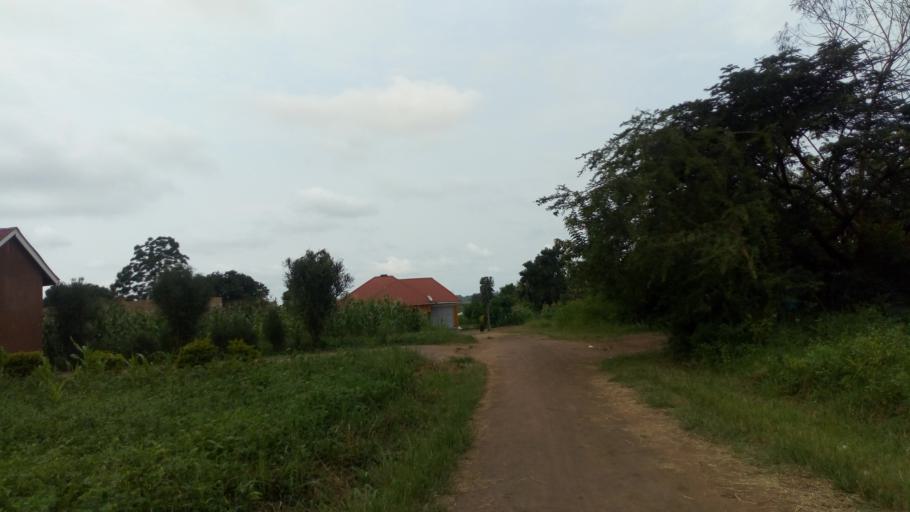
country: UG
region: Western Region
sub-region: Kiryandongo District
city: Kiryandongo
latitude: 1.7969
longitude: 32.0086
